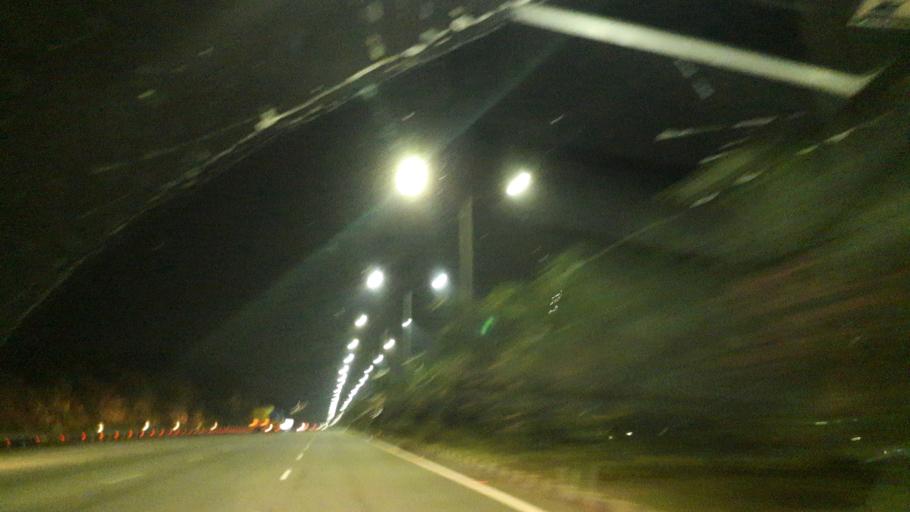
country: IN
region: Telangana
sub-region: Hyderabad
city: Hyderabad
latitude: 17.3183
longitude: 78.3762
